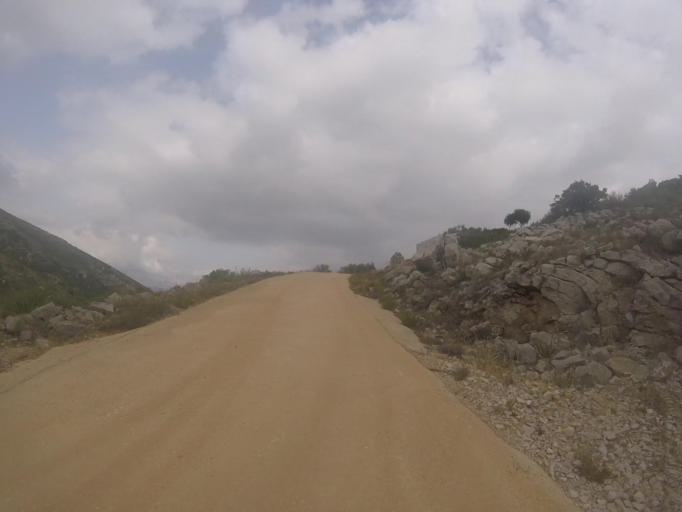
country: ES
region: Valencia
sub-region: Provincia de Castello
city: Santa Magdalena de Pulpis
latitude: 40.3452
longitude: 0.3229
